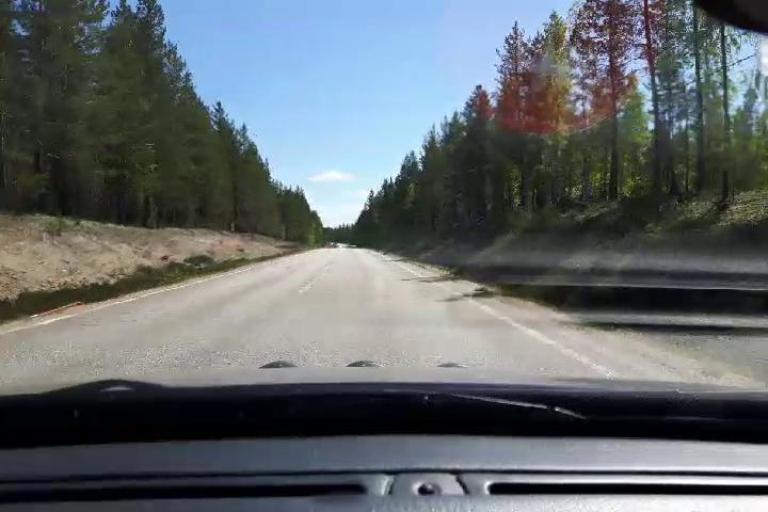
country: SE
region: Jaemtland
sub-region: Harjedalens Kommun
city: Sveg
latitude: 62.1205
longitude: 15.0385
